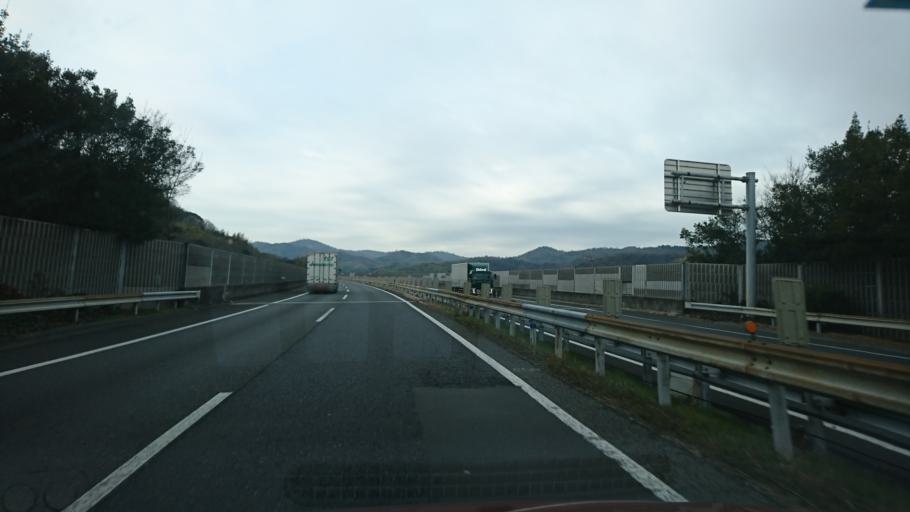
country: JP
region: Okayama
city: Kamogatacho-kamogata
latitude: 34.5519
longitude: 133.5791
